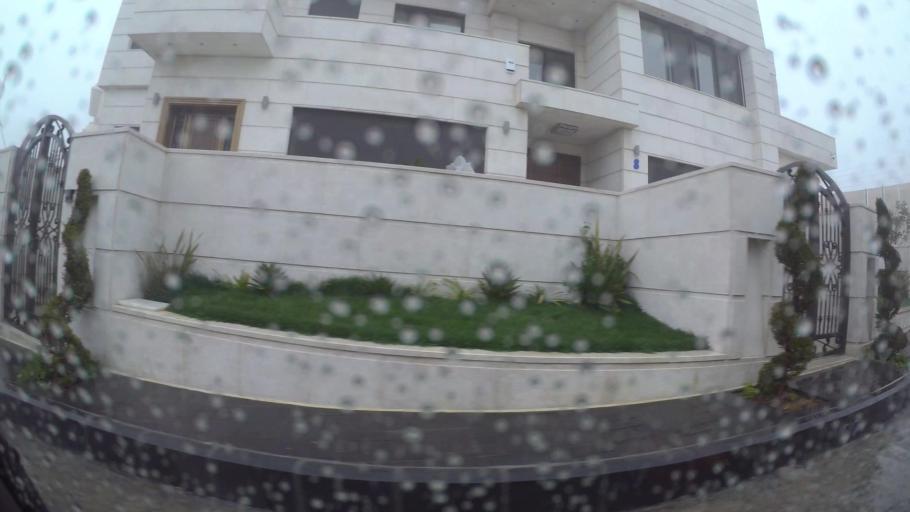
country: JO
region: Amman
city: Wadi as Sir
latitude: 31.9975
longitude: 35.8253
